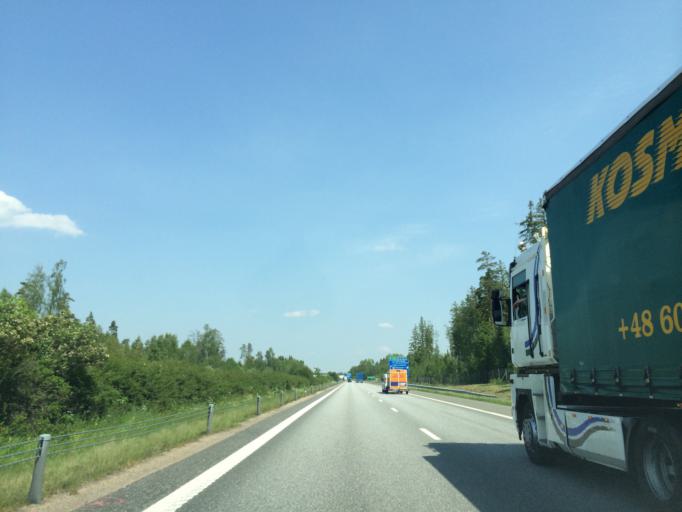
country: SE
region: Joenkoeping
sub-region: Varnamo Kommun
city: Varnamo
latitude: 57.1460
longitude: 14.0674
